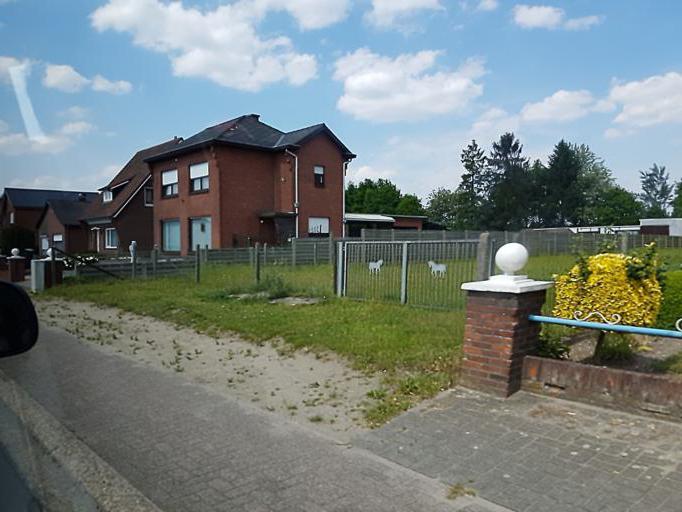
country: BE
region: Flanders
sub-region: Provincie Limburg
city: Bocholt
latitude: 51.1949
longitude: 5.5101
